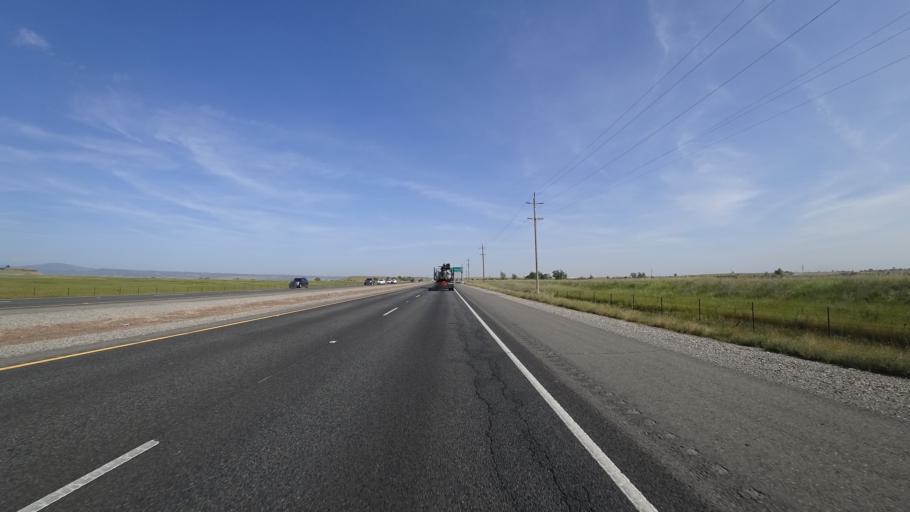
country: US
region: California
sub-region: Butte County
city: Durham
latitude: 39.6375
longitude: -121.7110
